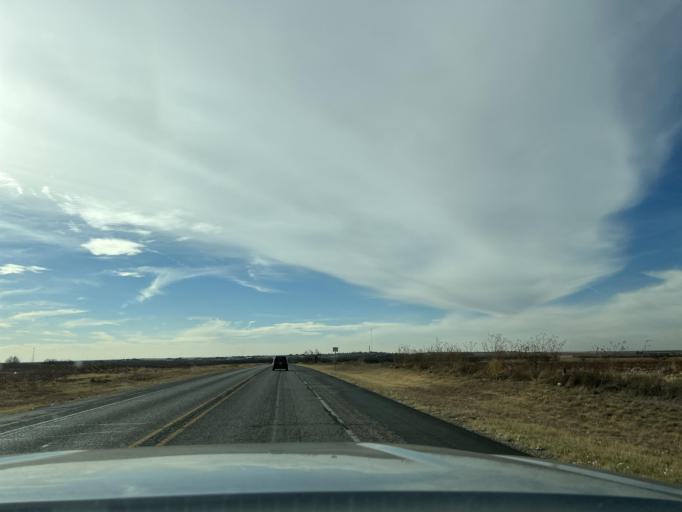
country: US
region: Texas
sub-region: Fisher County
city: Roby
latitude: 32.7508
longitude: -100.3492
